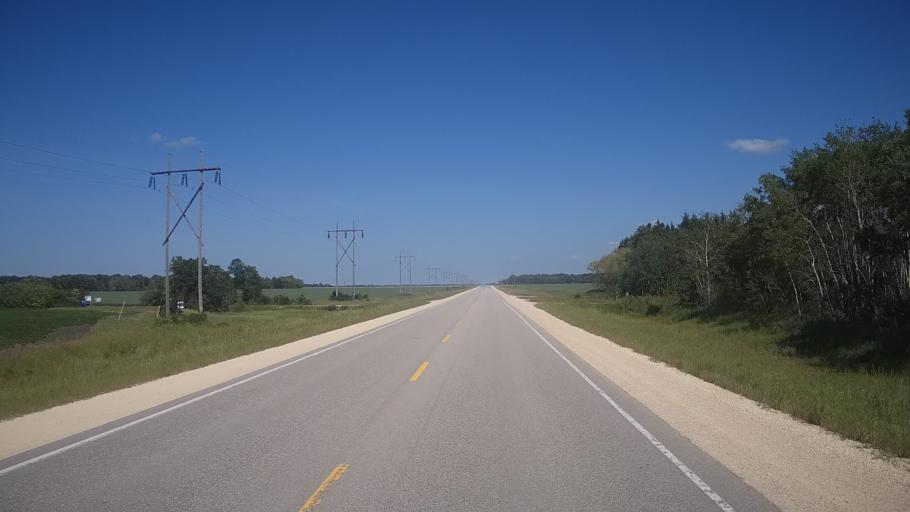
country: CA
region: Manitoba
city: Stonewall
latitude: 50.1227
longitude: -97.4498
